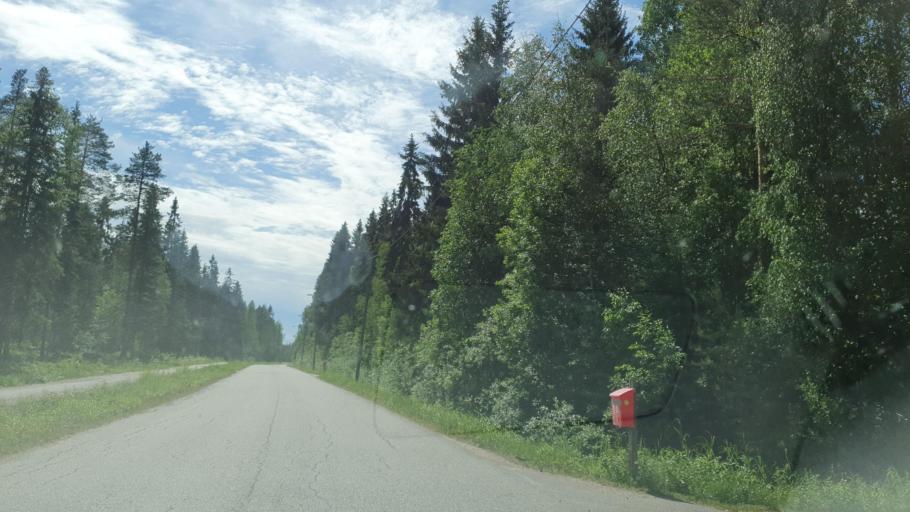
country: FI
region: Kainuu
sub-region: Kehys-Kainuu
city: Hyrynsalmi
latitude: 64.6861
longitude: 28.4663
